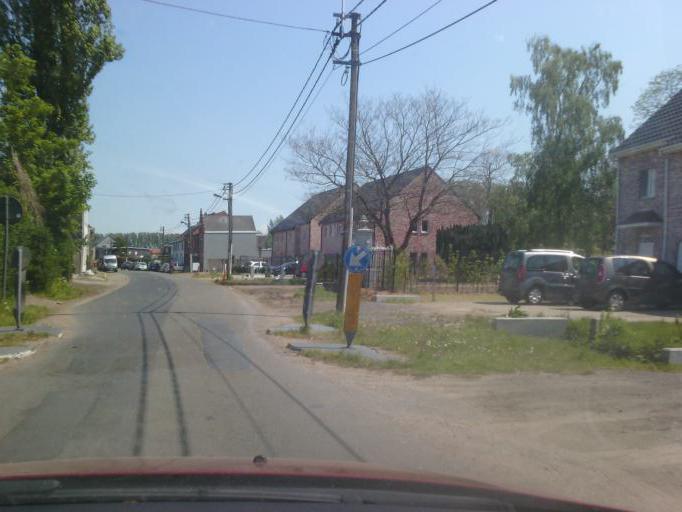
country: BE
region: Flanders
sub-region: Provincie Oost-Vlaanderen
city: Lokeren
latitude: 51.0906
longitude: 3.9815
